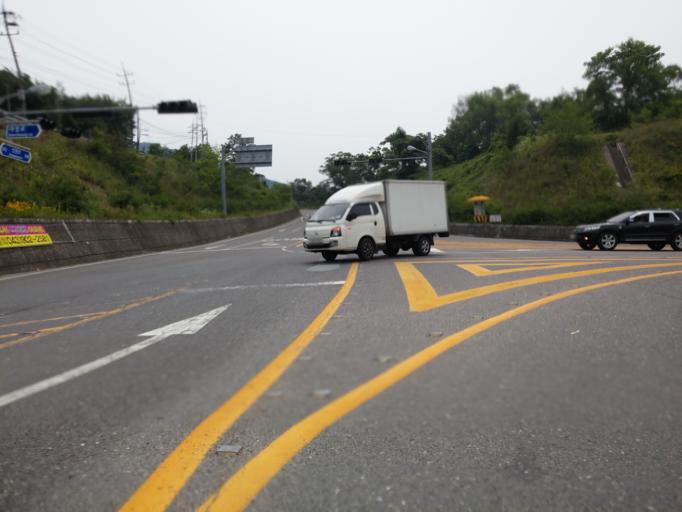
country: KR
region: Chungcheongbuk-do
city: Okcheon
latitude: 36.3057
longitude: 127.5499
